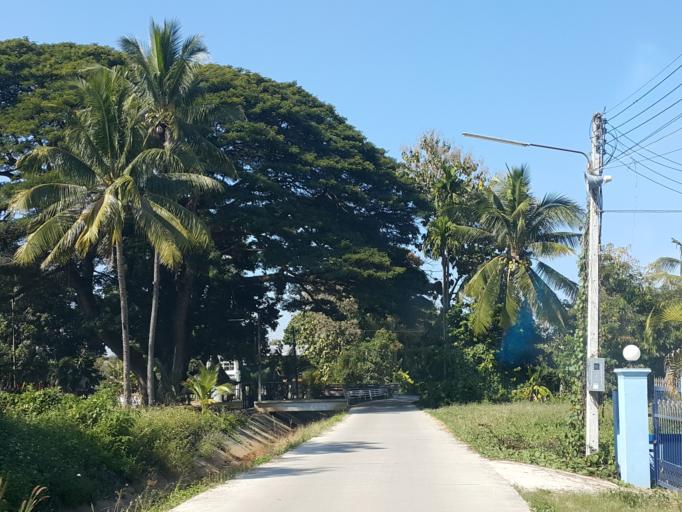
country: TH
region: Chiang Mai
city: San Sai
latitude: 18.8629
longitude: 98.9852
